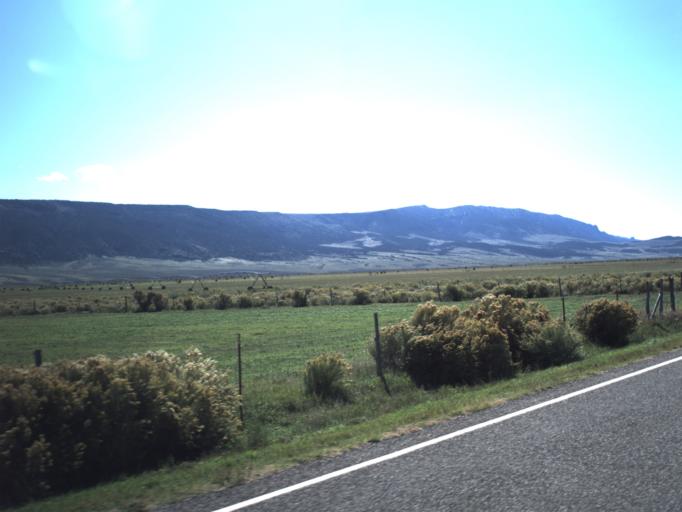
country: US
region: Utah
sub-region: Sevier County
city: Monroe
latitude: 38.4524
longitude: -111.9133
